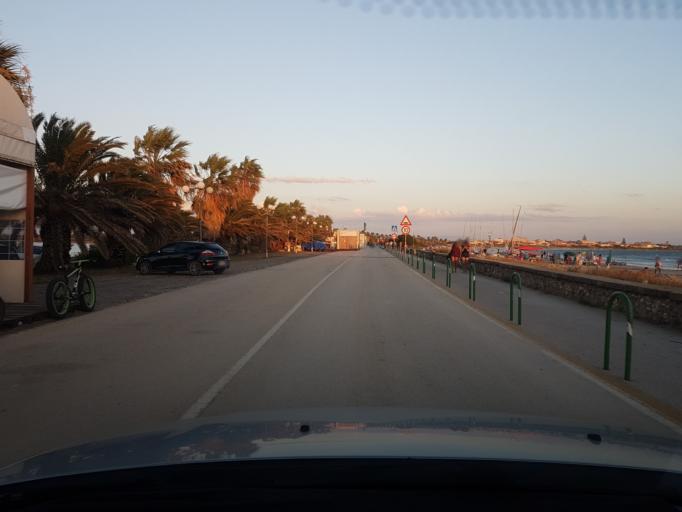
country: IT
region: Sardinia
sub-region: Provincia di Oristano
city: Riola Sardo
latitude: 40.0327
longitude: 8.4022
